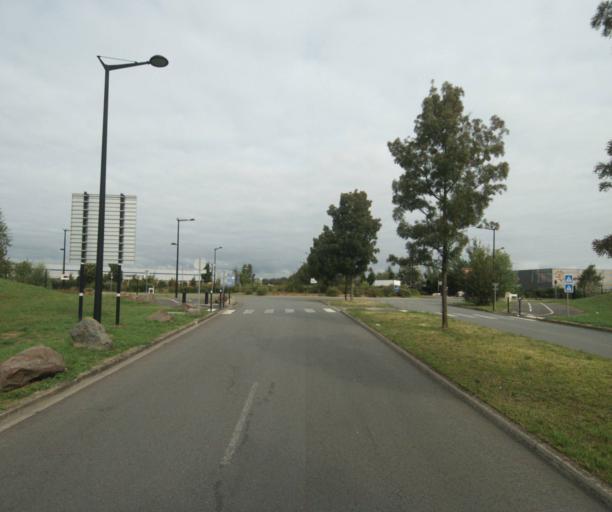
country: FR
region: Nord-Pas-de-Calais
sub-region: Departement du Nord
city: Lesquin
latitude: 50.5859
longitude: 3.1372
